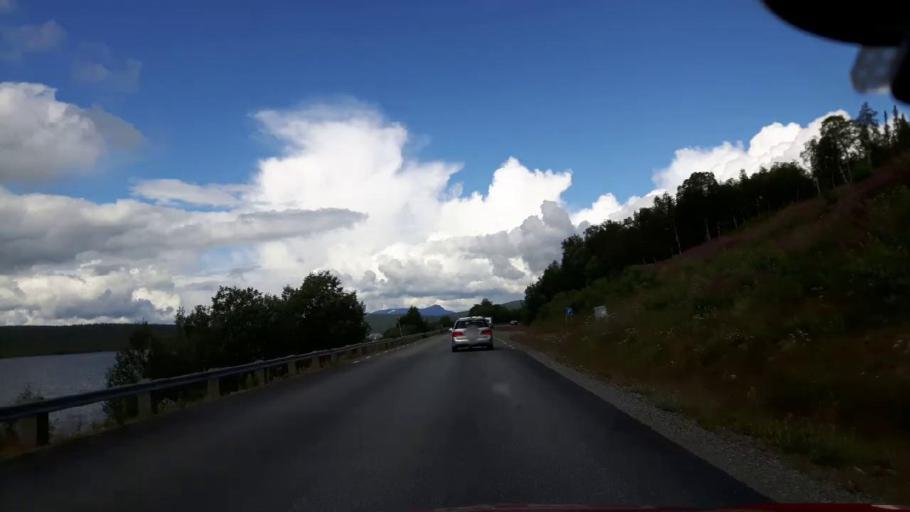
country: SE
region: Vaesterbotten
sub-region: Vilhelmina Kommun
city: Sjoberg
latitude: 65.0392
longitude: 15.1160
